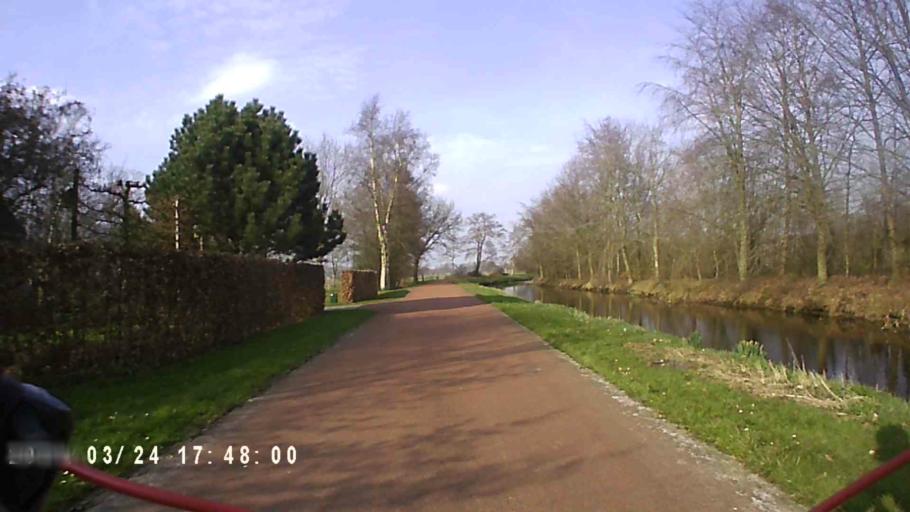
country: NL
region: Groningen
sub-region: Gemeente Leek
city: Leek
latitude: 53.1168
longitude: 6.3355
